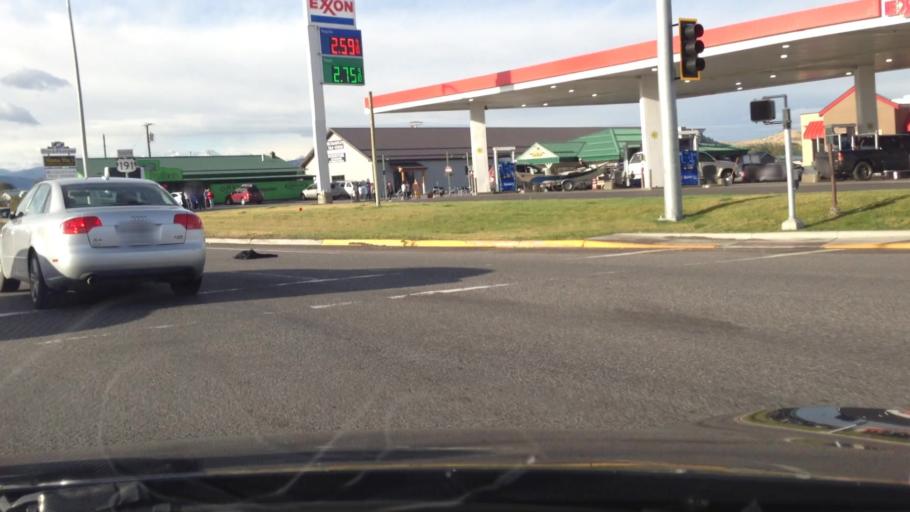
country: US
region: Montana
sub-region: Gallatin County
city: Four Corners
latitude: 45.6709
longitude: -111.1856
